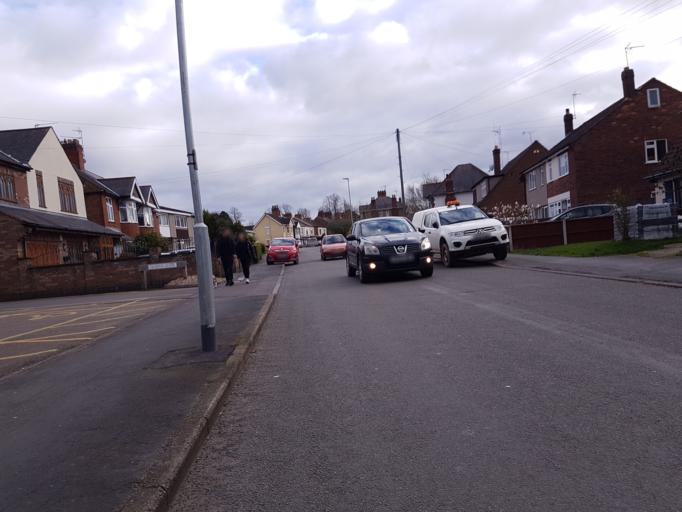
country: GB
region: England
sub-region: Leicestershire
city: Earl Shilton
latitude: 52.5733
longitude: -1.3167
